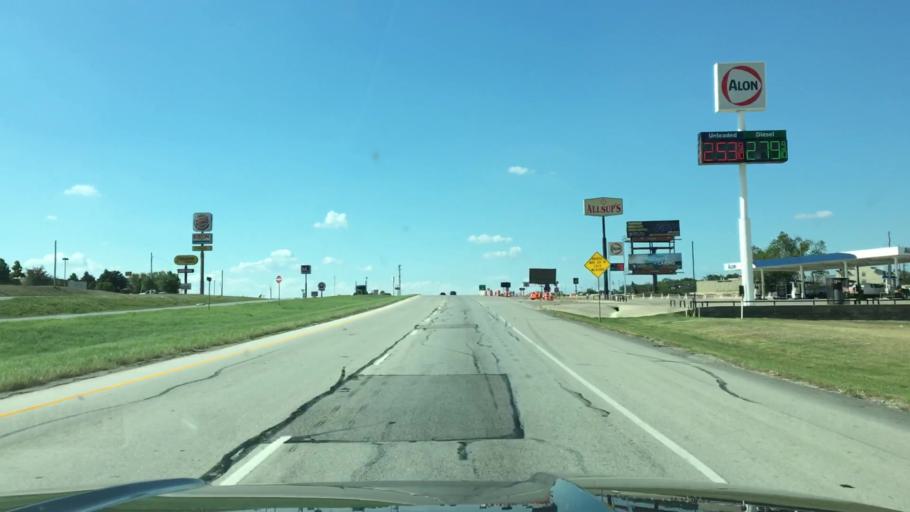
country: US
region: Texas
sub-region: Wise County
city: Decatur
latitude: 33.2245
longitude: -97.5913
